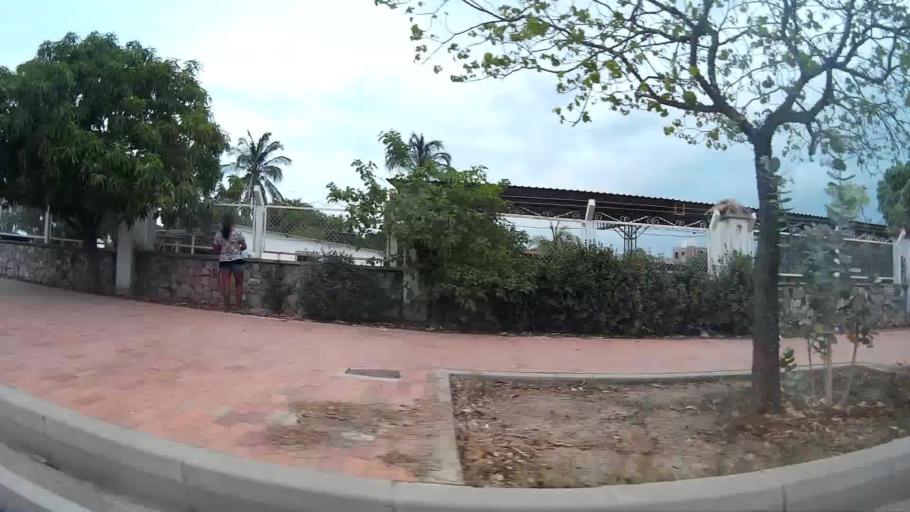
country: CO
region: Magdalena
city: Santa Marta
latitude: 11.1276
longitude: -74.2280
